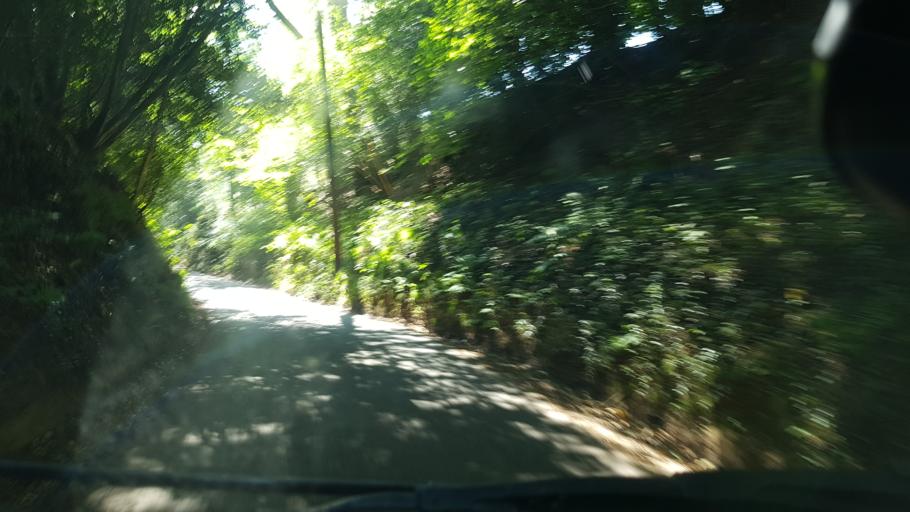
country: GB
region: England
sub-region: Surrey
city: Cranleigh
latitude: 51.1704
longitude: -0.4862
